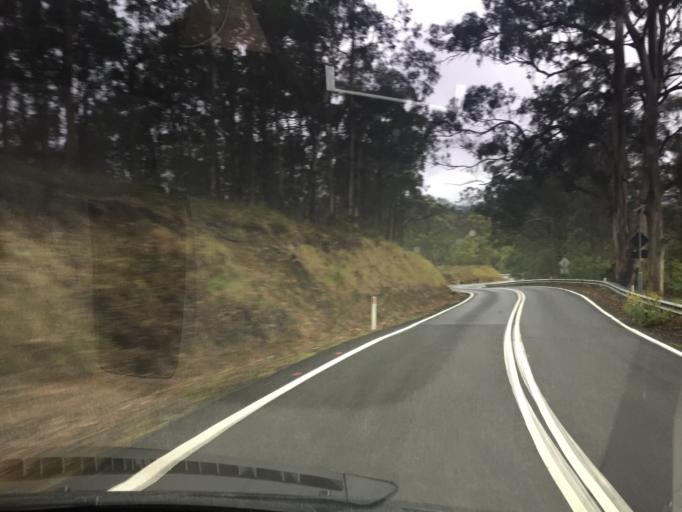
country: AU
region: New South Wales
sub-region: Bega Valley
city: Bega
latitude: -36.6114
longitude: 149.4772
